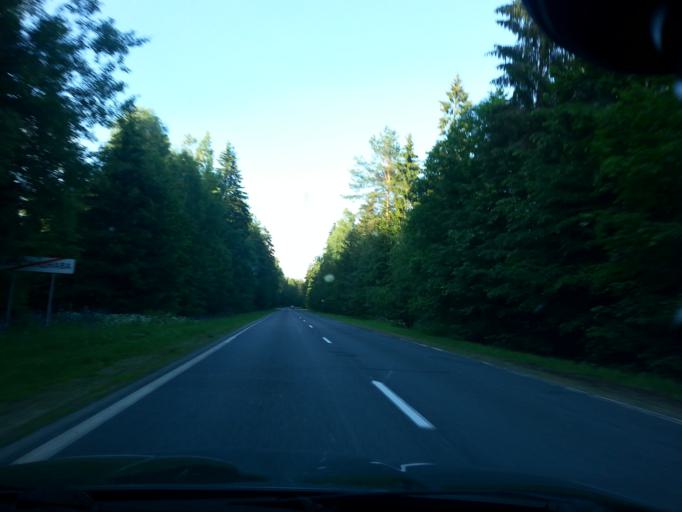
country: BY
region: Minsk
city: Svir
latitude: 54.9216
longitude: 26.4664
